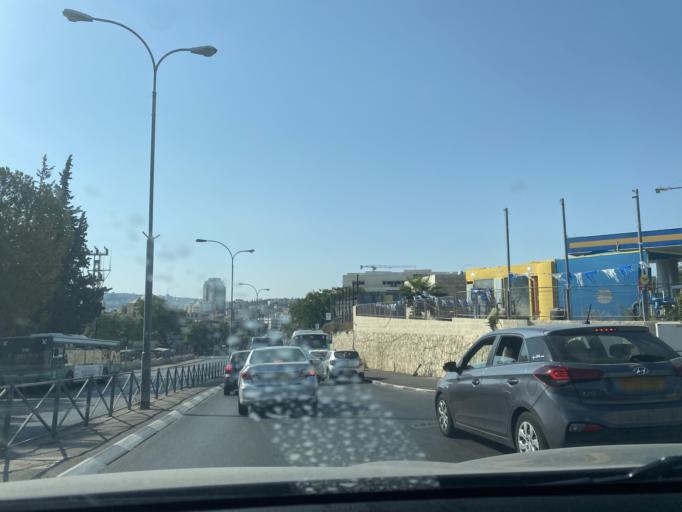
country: IL
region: Jerusalem
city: Jerusalem
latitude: 31.7473
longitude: 35.2125
